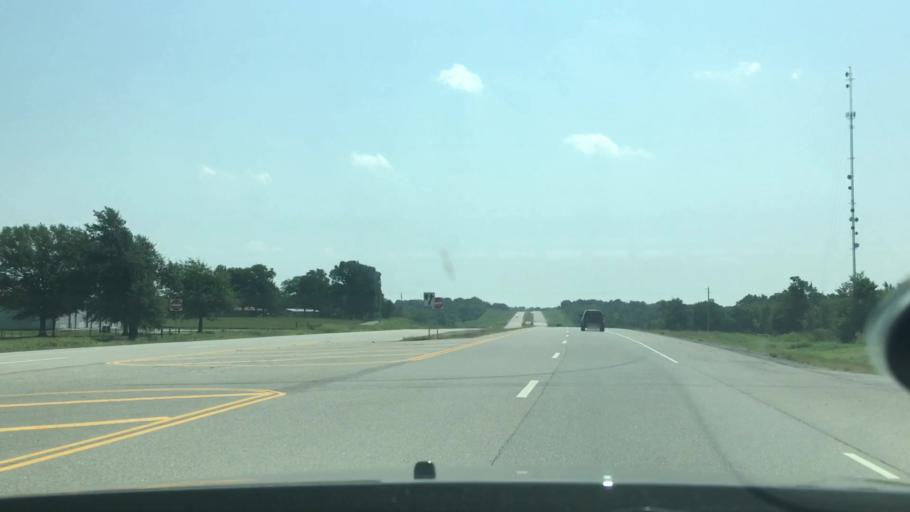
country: US
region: Oklahoma
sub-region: Atoka County
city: Atoka
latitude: 34.3582
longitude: -96.0925
